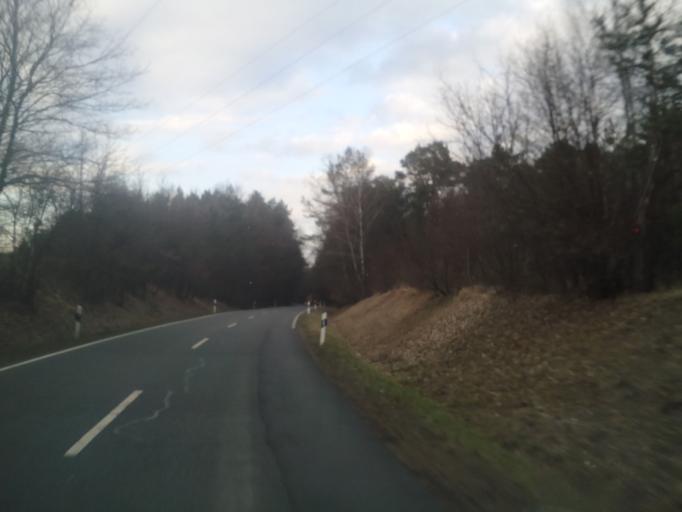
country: DE
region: Bavaria
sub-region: Upper Franconia
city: Pommersfelden
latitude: 49.7373
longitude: 10.8169
